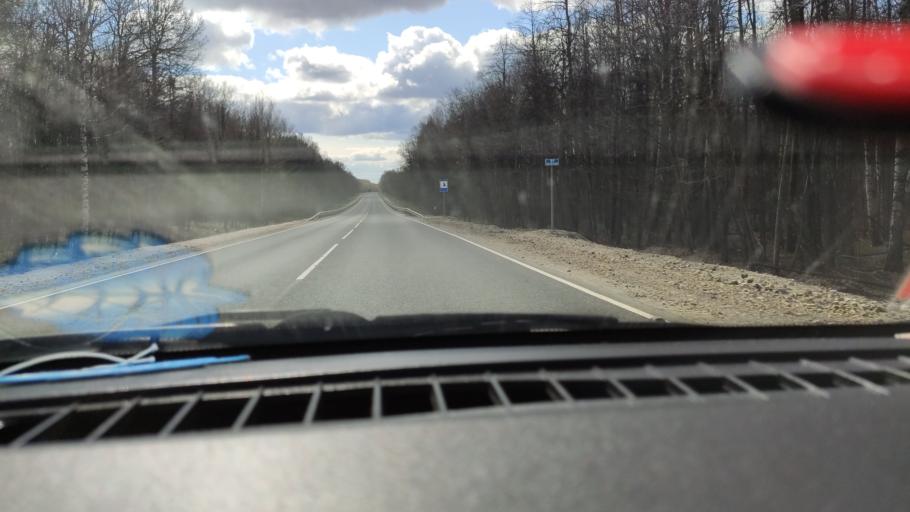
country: RU
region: Saratov
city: Khvalynsk
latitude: 52.4677
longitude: 48.0167
